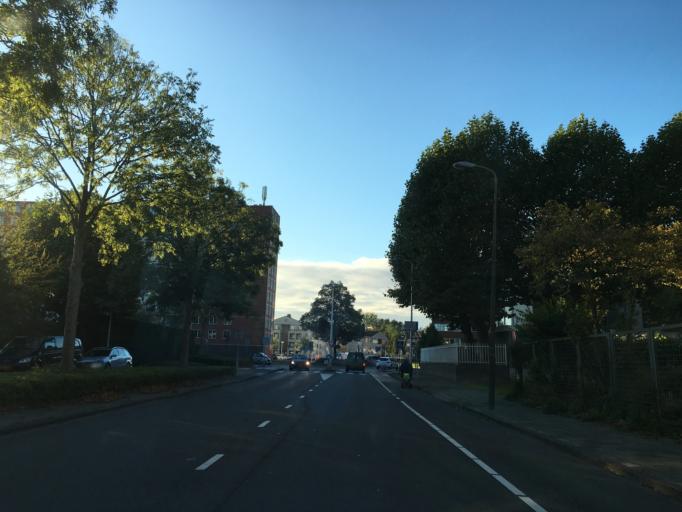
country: NL
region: South Holland
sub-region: Gemeente Capelle aan den IJssel
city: Capelle aan den IJssel
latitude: 51.9253
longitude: 4.5811
